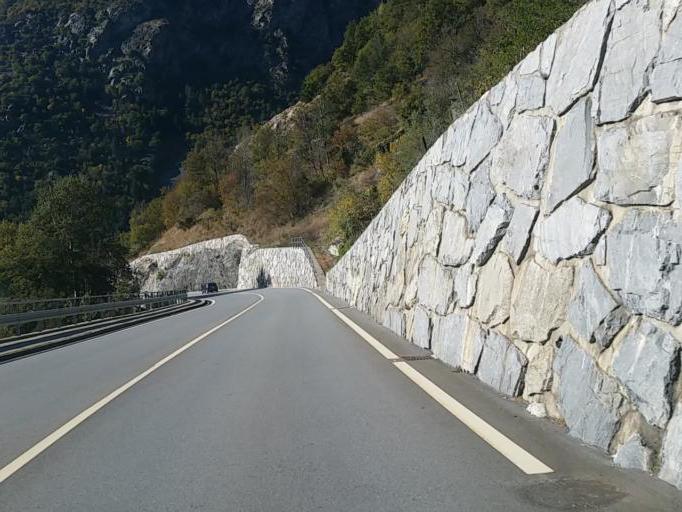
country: CH
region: Valais
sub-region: Leuk District
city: Gampel
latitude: 46.3174
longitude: 7.7491
